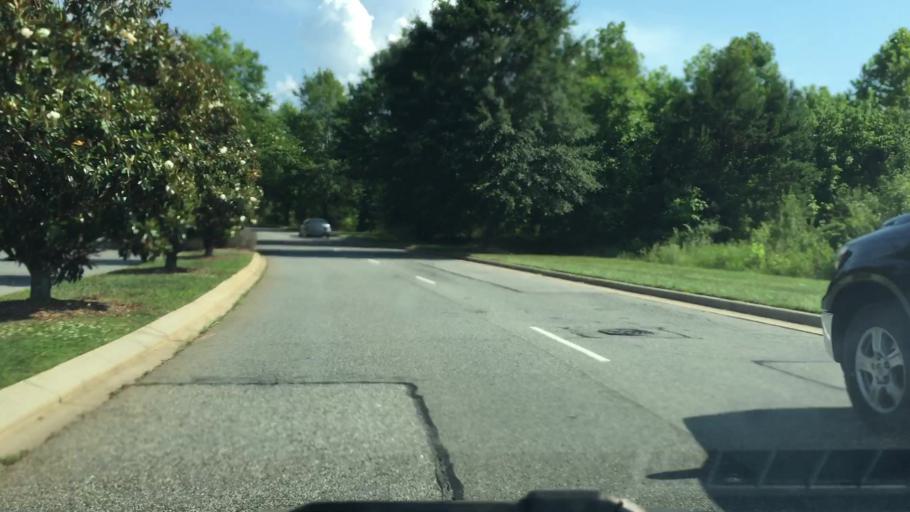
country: US
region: North Carolina
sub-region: Iredell County
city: Mooresville
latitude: 35.5850
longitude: -80.8828
